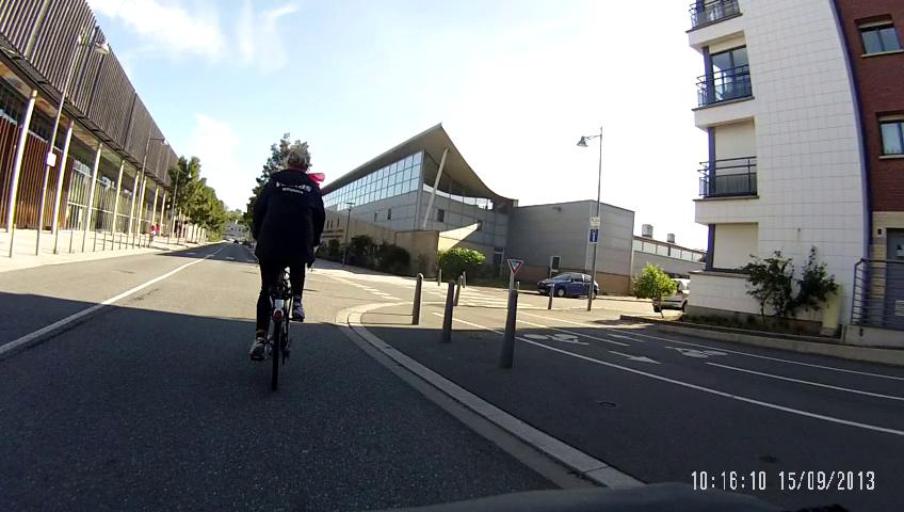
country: FR
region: Nord-Pas-de-Calais
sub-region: Departement du Nord
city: Dunkerque
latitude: 51.0431
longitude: 2.3798
